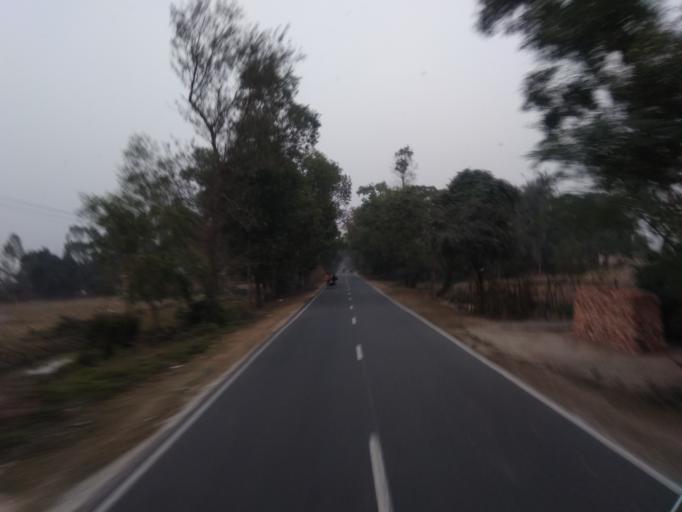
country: BD
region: Rajshahi
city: Bogra
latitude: 24.6529
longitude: 89.2603
